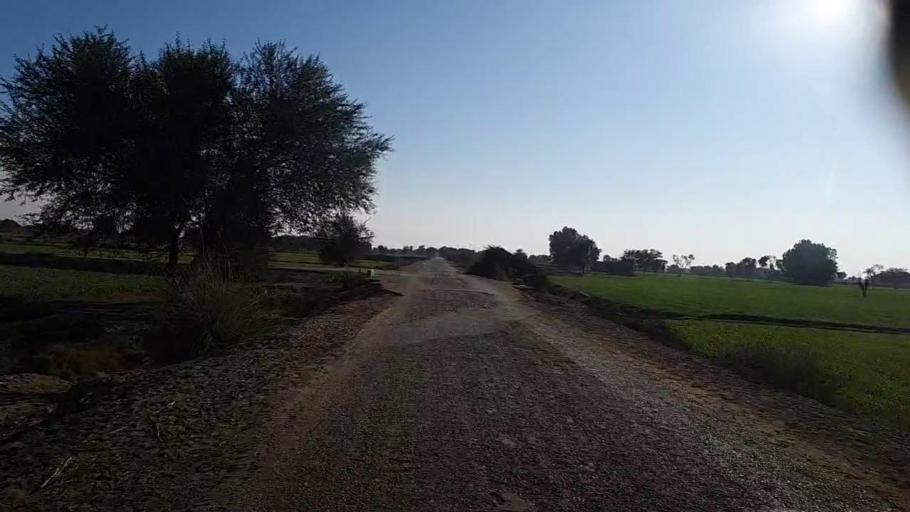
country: PK
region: Sindh
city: Khairpur
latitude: 27.8927
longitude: 69.7461
